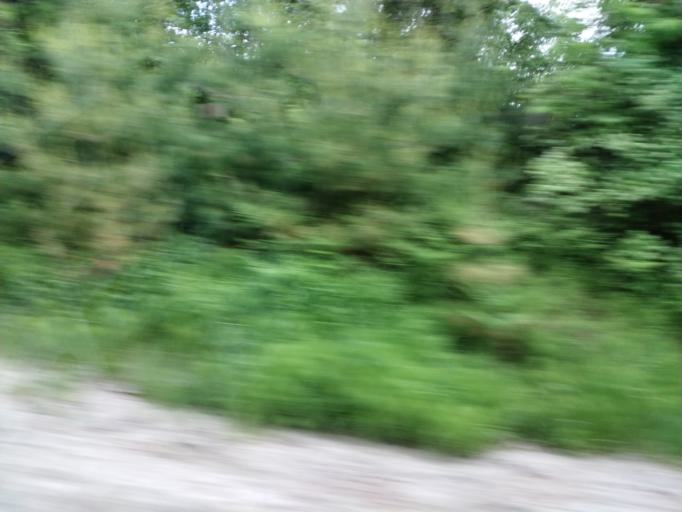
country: US
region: Maine
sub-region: Cumberland County
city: New Gloucester
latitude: 43.8923
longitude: -70.2722
